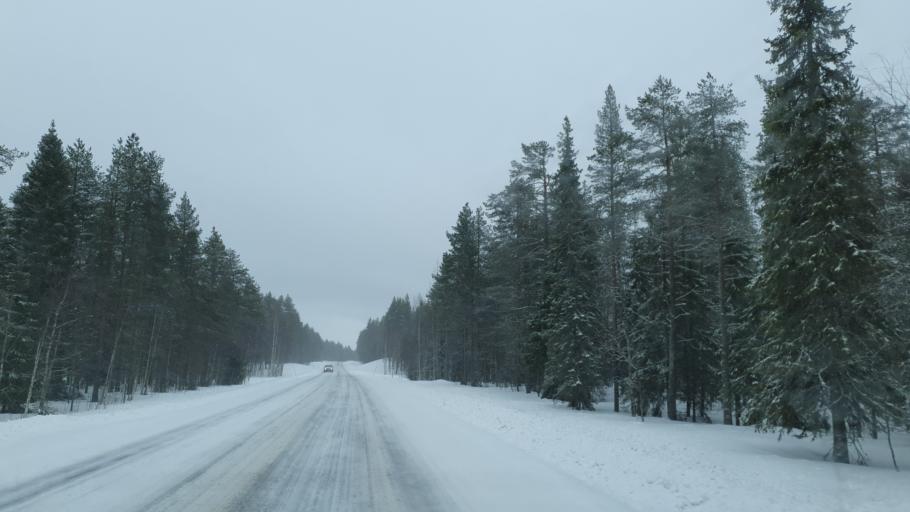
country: FI
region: Lapland
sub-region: Rovaniemi
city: Ranua
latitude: 66.1760
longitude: 26.2297
